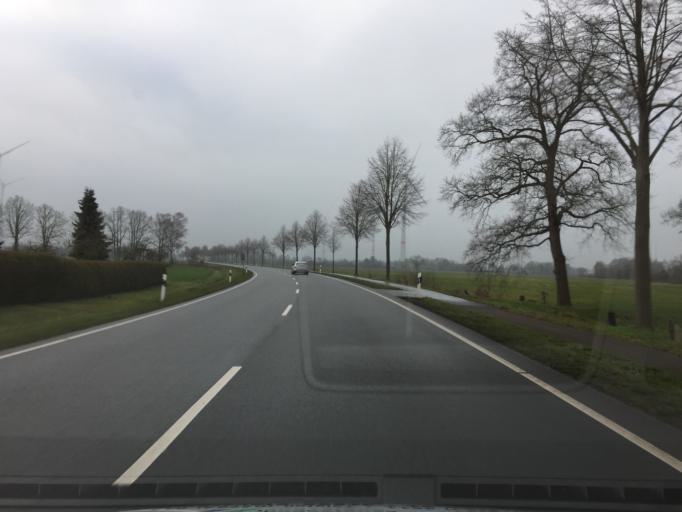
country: DE
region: Lower Saxony
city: Sulingen
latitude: 52.6527
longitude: 8.8061
